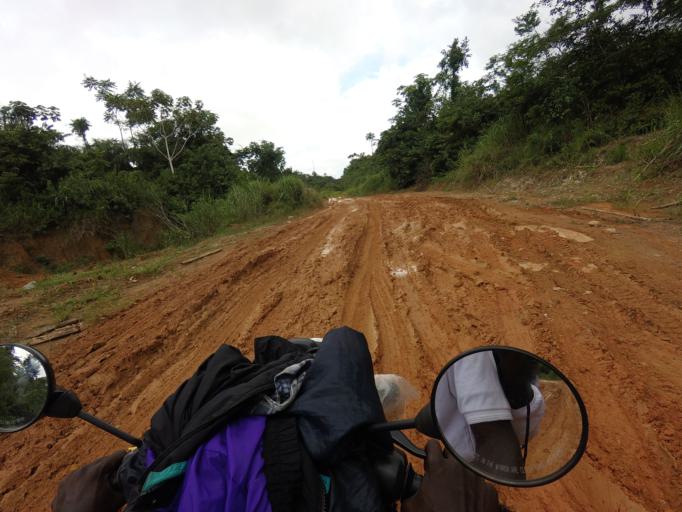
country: SL
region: Eastern Province
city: Tombodu
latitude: 8.1613
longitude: -10.6564
